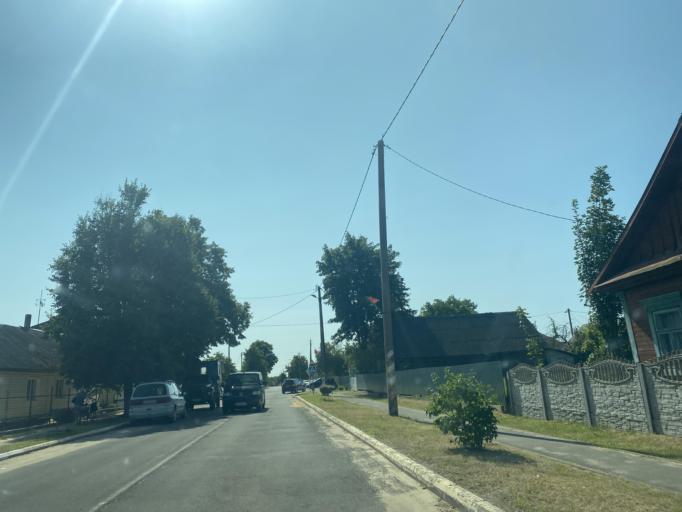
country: BY
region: Brest
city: Ivanava
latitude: 52.3156
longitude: 25.6117
